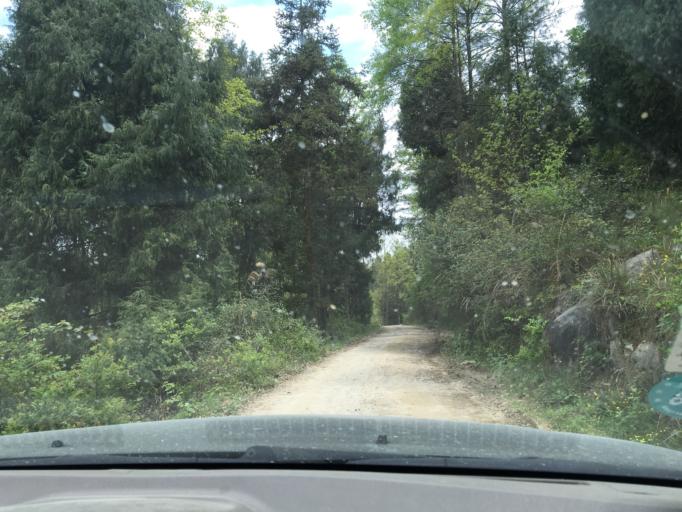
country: CN
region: Guizhou Sheng
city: Kuanping
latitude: 28.0237
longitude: 108.0650
